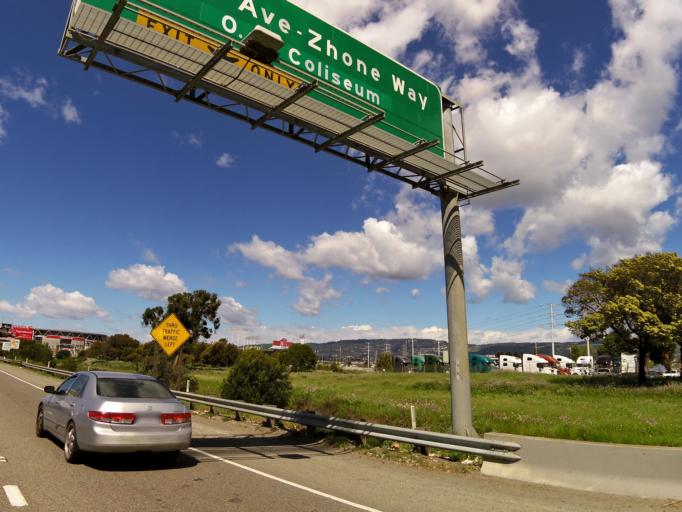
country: US
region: California
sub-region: Alameda County
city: Alameda
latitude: 37.7444
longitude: -122.1995
